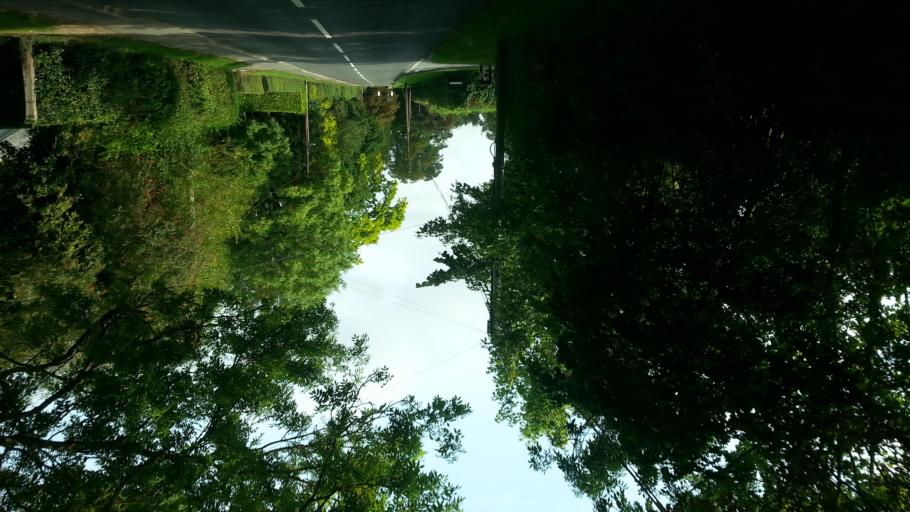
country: GB
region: England
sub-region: Cambridgeshire
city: Comberton
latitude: 52.2096
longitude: 0.0102
